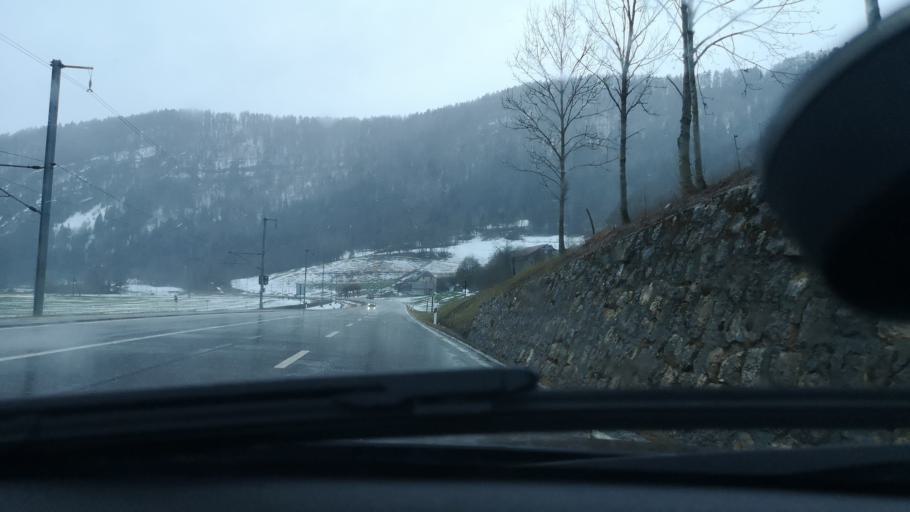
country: CH
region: Neuchatel
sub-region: Val-de-Travers District
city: Travers
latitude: 46.9569
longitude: 6.7080
